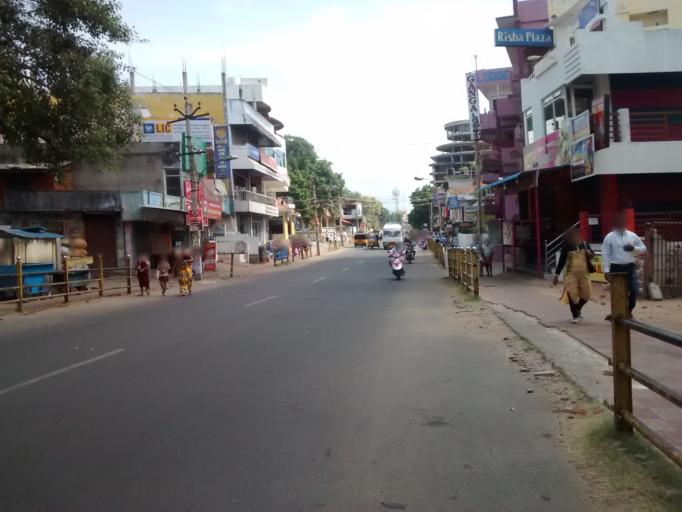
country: IN
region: Tamil Nadu
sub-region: Kanniyakumari
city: Kanniyakumari
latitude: 8.0849
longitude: 77.5495
